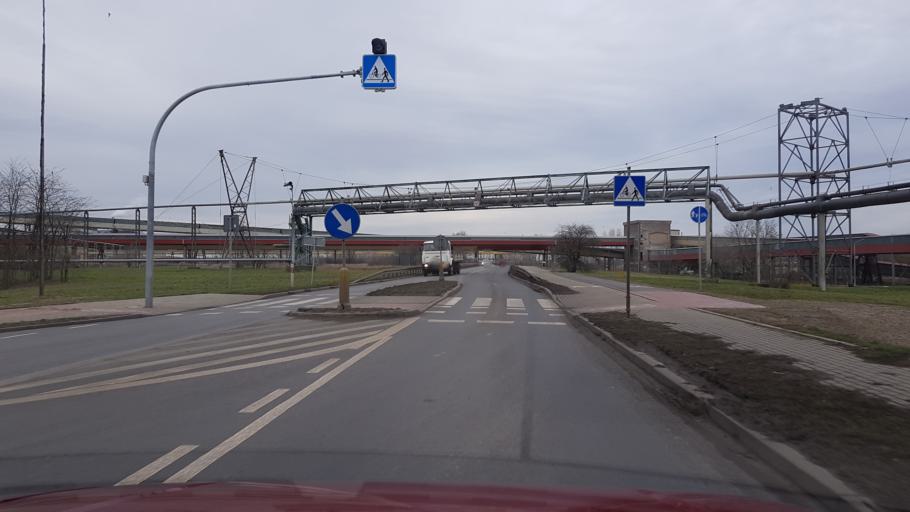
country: PL
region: West Pomeranian Voivodeship
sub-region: Powiat policki
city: Police
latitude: 53.5716
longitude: 14.5563
